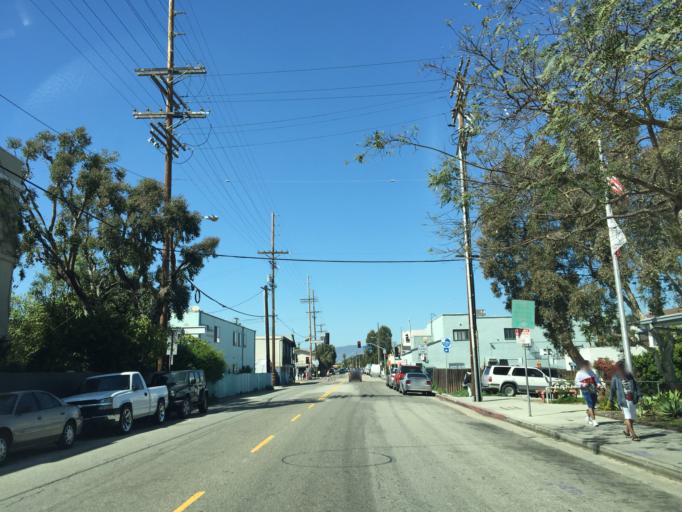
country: US
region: California
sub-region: Los Angeles County
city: Marina del Rey
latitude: 33.9789
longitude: -118.4650
